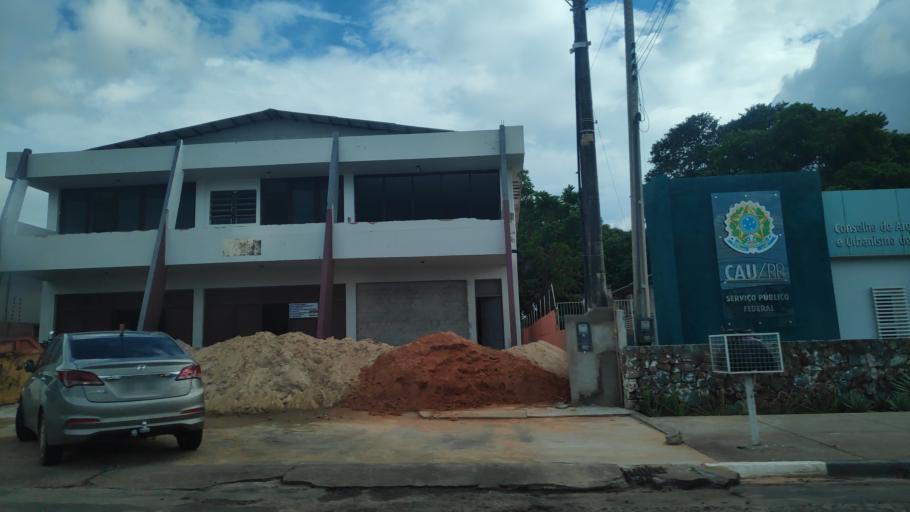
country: BR
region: Roraima
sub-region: Boa Vista
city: Boa Vista
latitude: 2.8273
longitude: -60.6683
